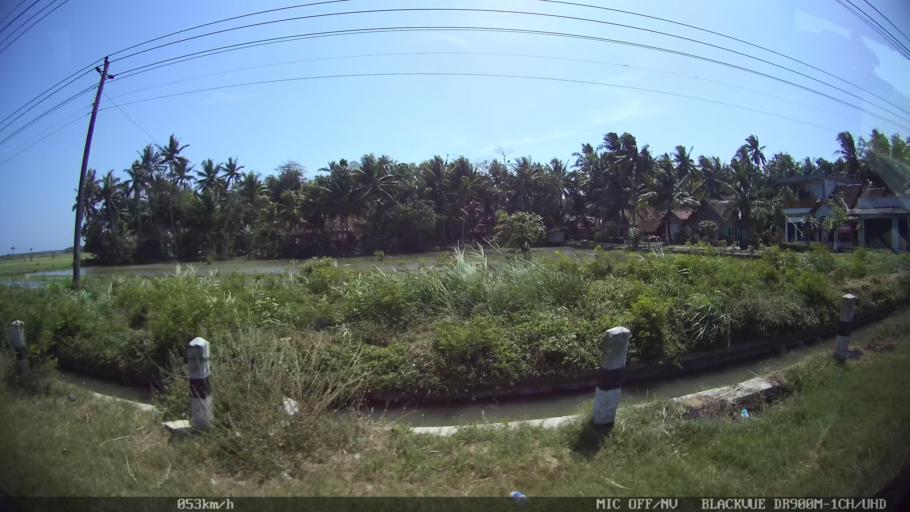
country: ID
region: Daerah Istimewa Yogyakarta
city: Srandakan
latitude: -7.9527
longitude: 110.1961
